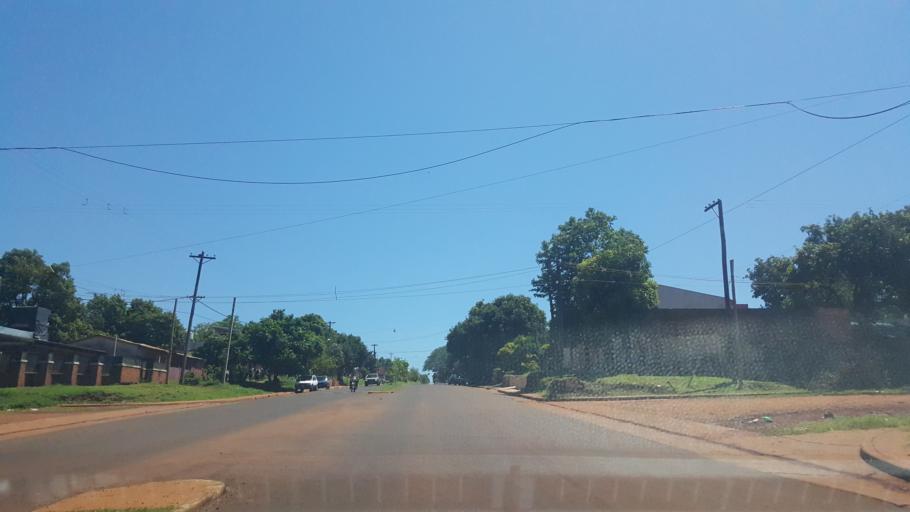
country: AR
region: Misiones
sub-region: Departamento de Capital
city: Posadas
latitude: -27.3914
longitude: -55.9312
